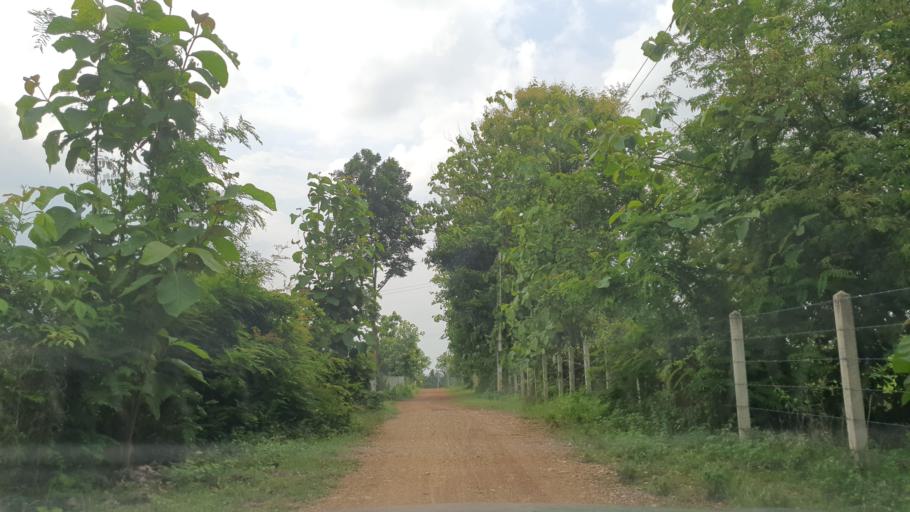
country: TH
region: Sukhothai
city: Thung Saliam
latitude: 17.2452
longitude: 99.5439
